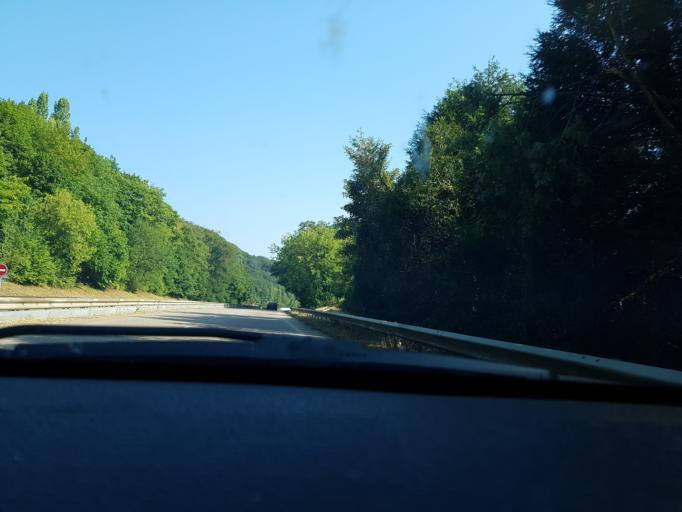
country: FR
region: Lorraine
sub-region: Departement de Meurthe-et-Moselle
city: Maxeville
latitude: 48.7097
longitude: 6.1614
